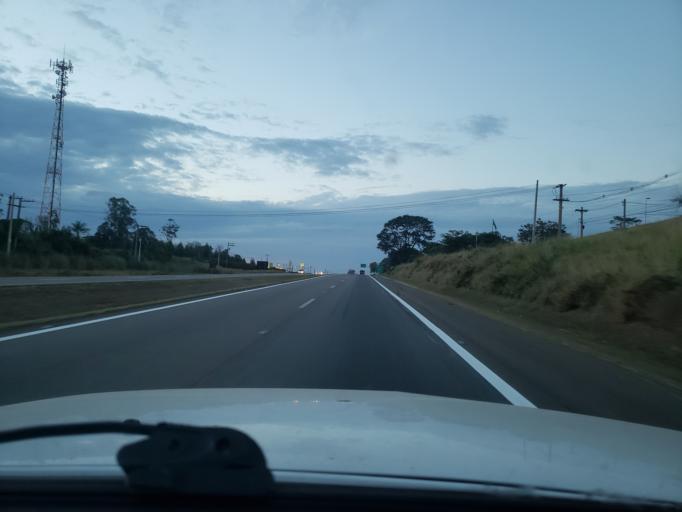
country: BR
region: Sao Paulo
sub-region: Mogi-Mirim
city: Mogi Mirim
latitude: -22.4839
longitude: -46.9810
